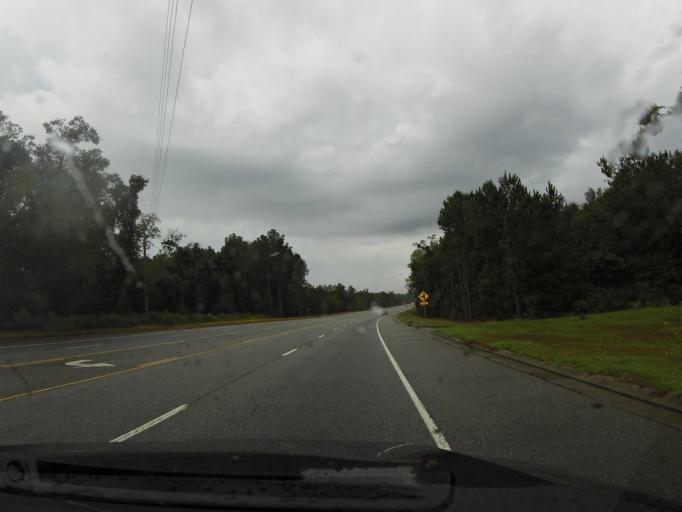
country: US
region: Georgia
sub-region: Wayne County
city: Jesup
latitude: 31.5623
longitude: -81.8350
